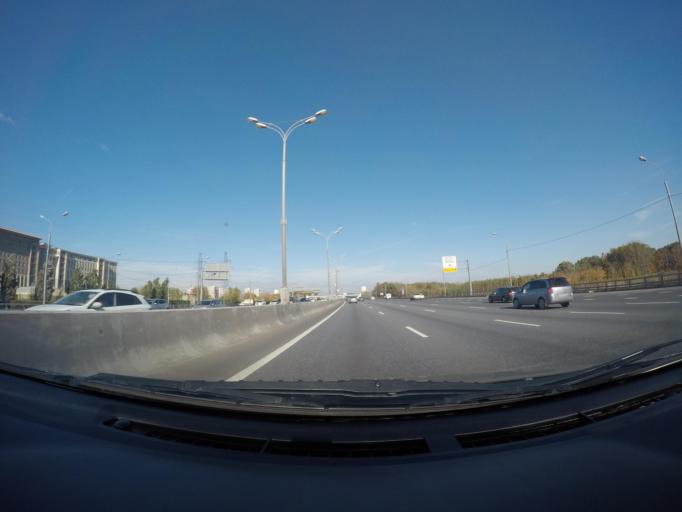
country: RU
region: Moscow
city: Zhulebino
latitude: 55.7148
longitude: 37.8386
